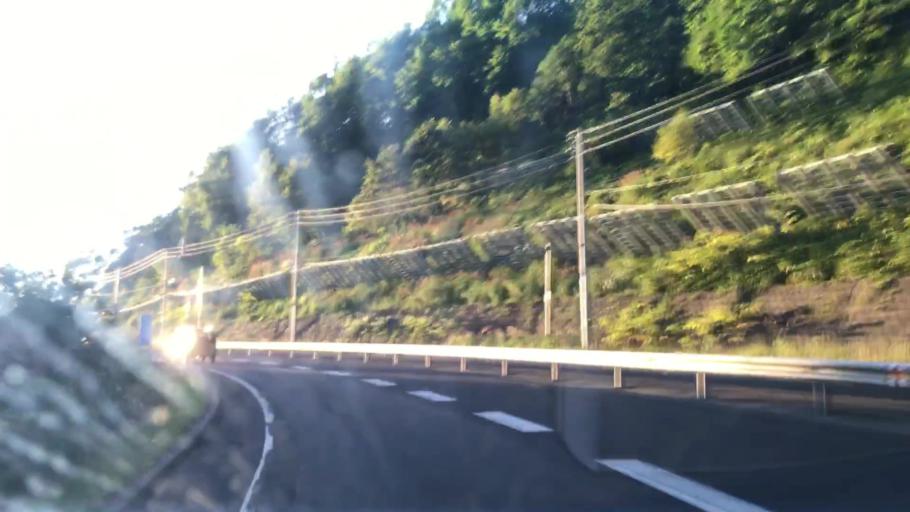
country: JP
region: Hokkaido
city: Otaru
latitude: 42.8470
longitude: 141.0699
